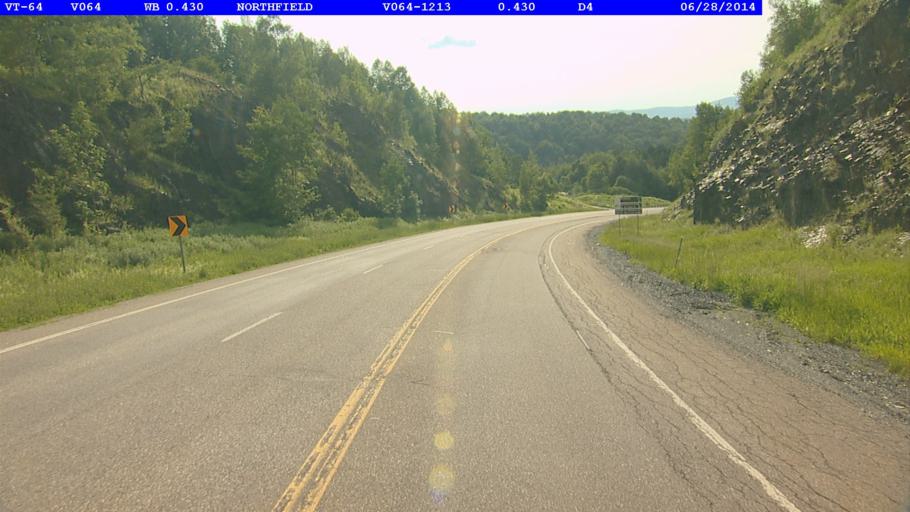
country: US
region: Vermont
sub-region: Washington County
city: Northfield
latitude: 44.1158
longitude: -72.6491
